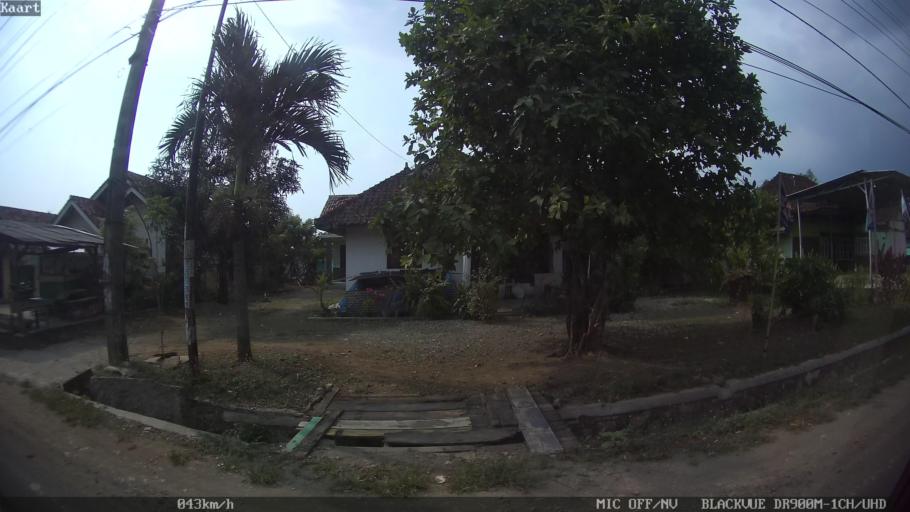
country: ID
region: Lampung
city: Gadingrejo
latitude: -5.3783
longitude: 105.0318
